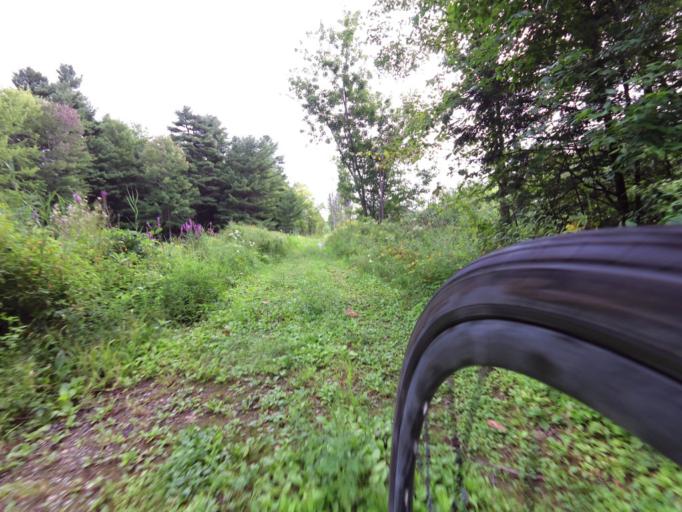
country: CA
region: Ontario
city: Gananoque
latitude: 44.6044
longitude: -76.2875
